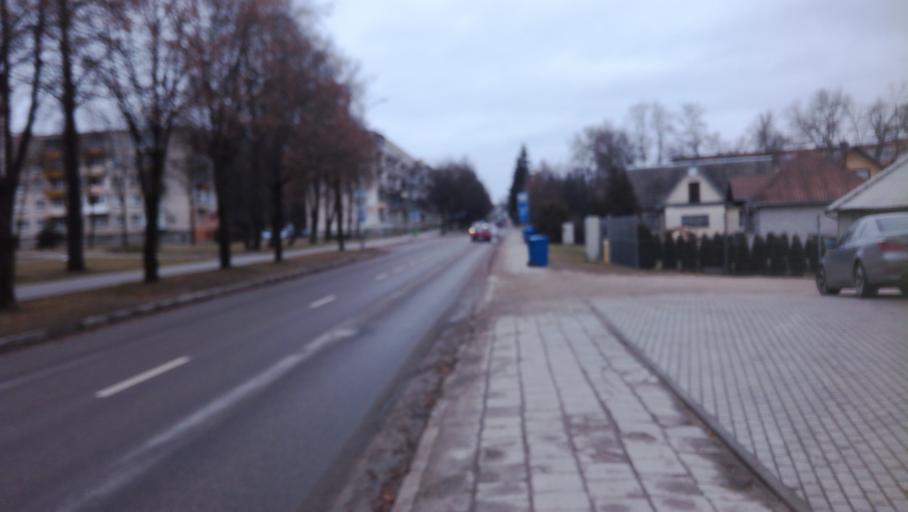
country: LT
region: Alytaus apskritis
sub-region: Alytus
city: Alytus
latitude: 54.3973
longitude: 24.0384
